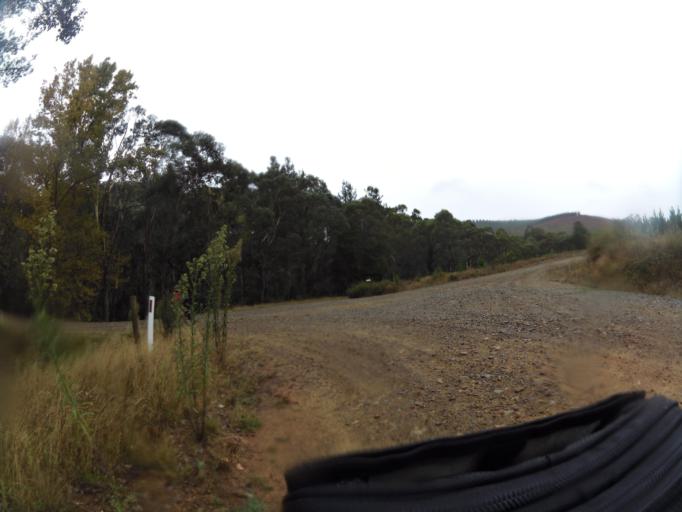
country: AU
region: New South Wales
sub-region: Greater Hume Shire
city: Holbrook
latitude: -36.2101
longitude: 147.5729
